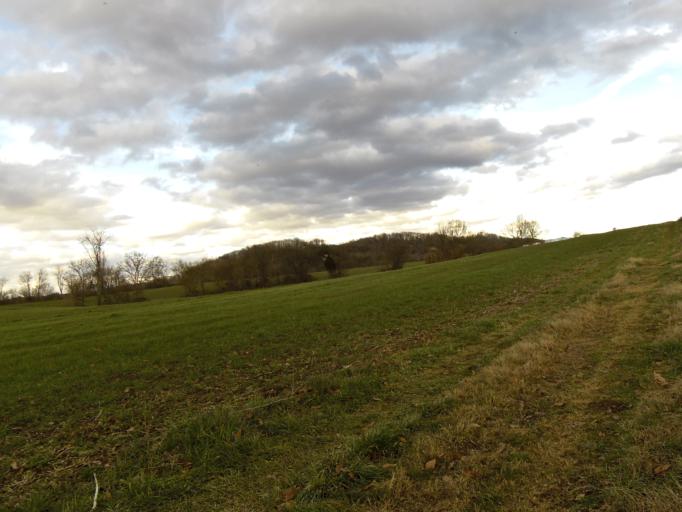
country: US
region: Tennessee
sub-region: Knox County
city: Knoxville
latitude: 35.9541
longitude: -83.8499
